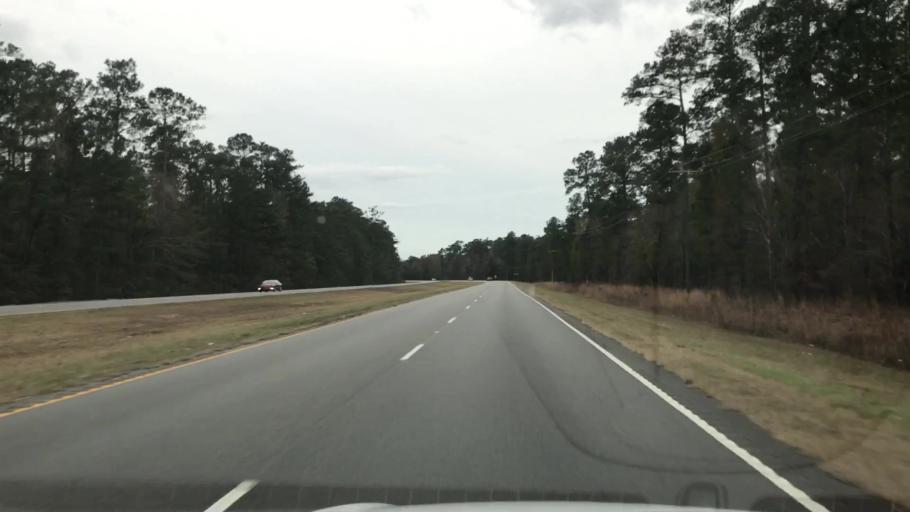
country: US
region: South Carolina
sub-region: Georgetown County
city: Georgetown
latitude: 33.2556
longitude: -79.3714
